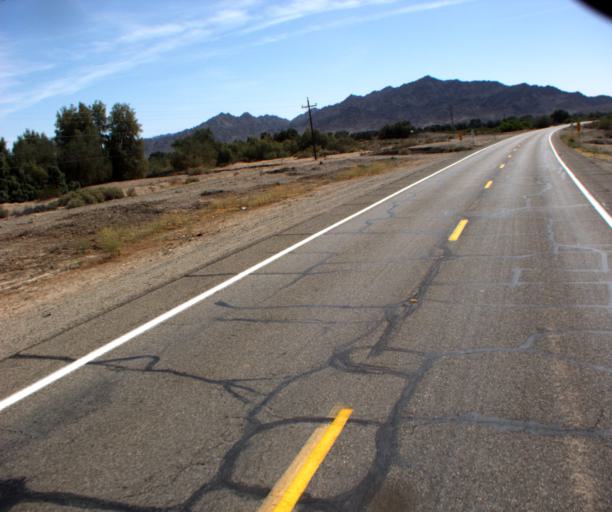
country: US
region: Arizona
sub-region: Yuma County
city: Fortuna Foothills
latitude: 32.7828
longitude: -114.3820
